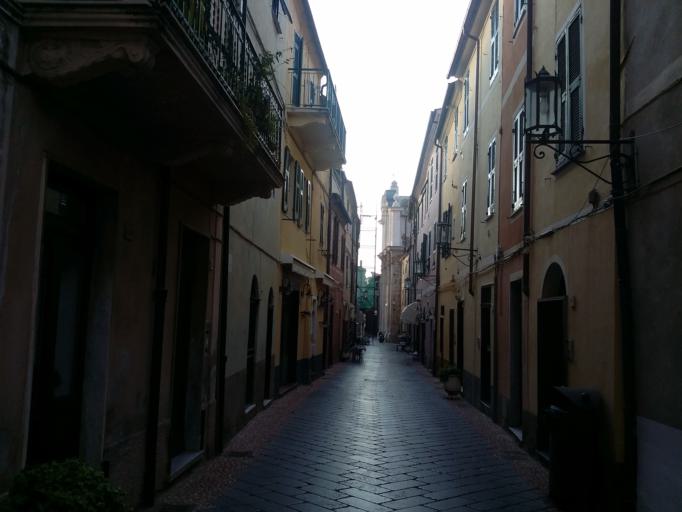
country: IT
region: Liguria
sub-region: Provincia di Savona
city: Noli
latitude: 44.2057
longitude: 8.4136
